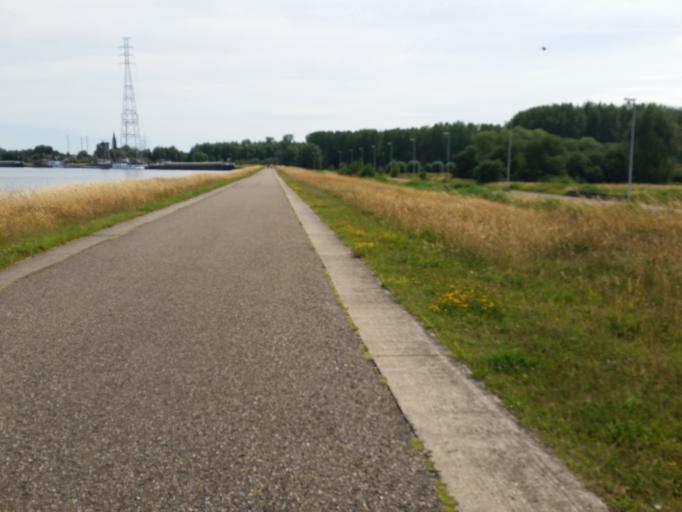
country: BE
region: Flanders
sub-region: Provincie Antwerpen
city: Niel
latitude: 51.1153
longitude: 4.2997
